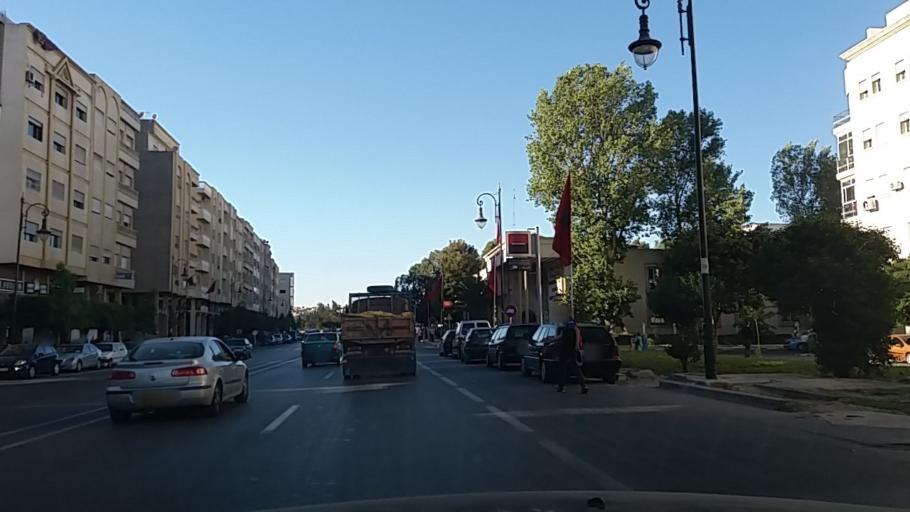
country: MA
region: Tanger-Tetouan
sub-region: Tanger-Assilah
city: Tangier
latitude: 35.7467
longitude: -5.7987
